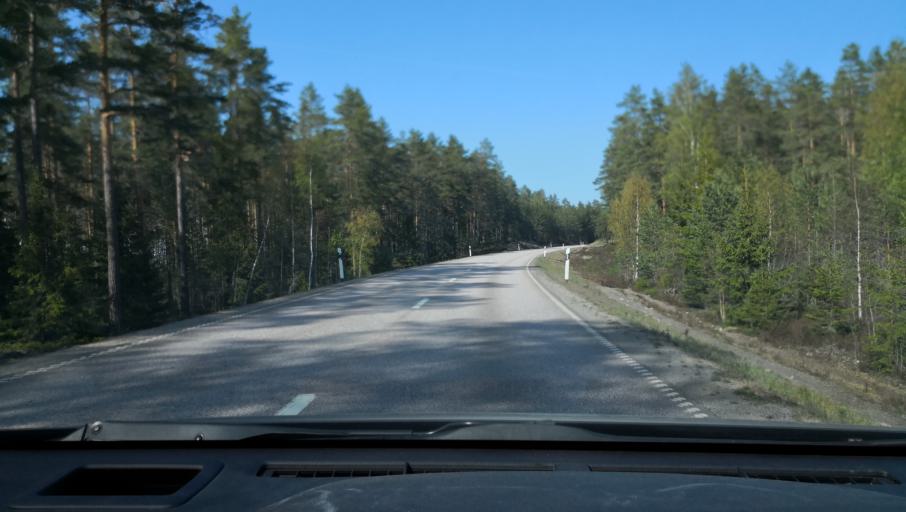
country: SE
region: Uppsala
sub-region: Heby Kommun
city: Tarnsjo
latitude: 60.0559
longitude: 16.8661
